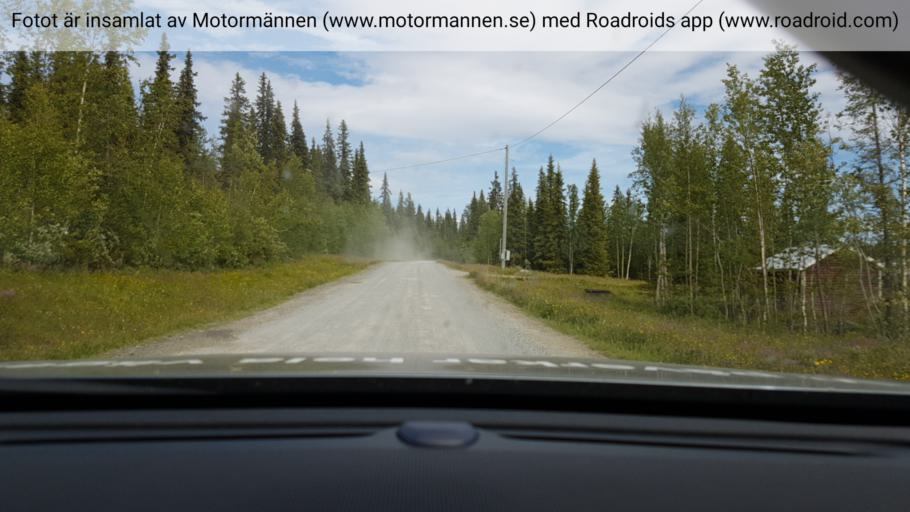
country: SE
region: Vaesterbotten
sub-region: Vilhelmina Kommun
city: Sjoberg
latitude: 65.1990
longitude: 16.1399
